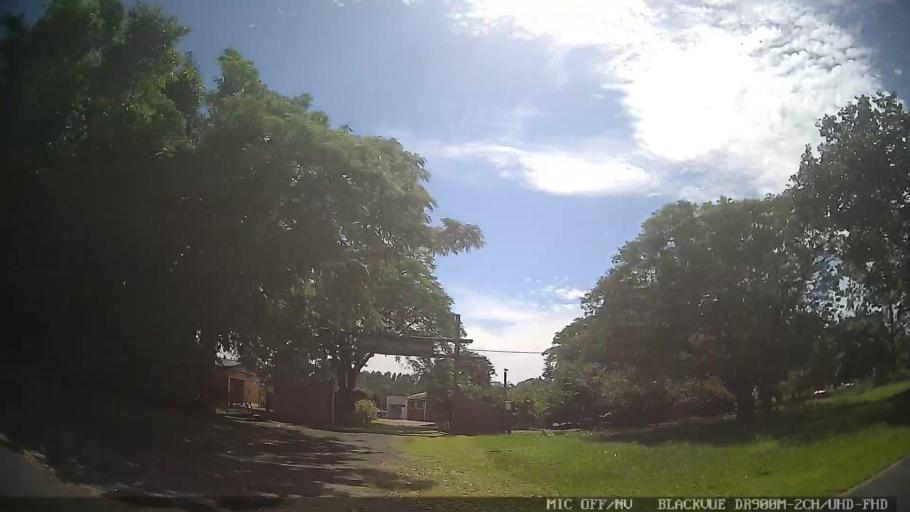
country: BR
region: Sao Paulo
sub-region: Cerquilho
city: Cerquilho
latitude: -23.1778
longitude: -47.6403
